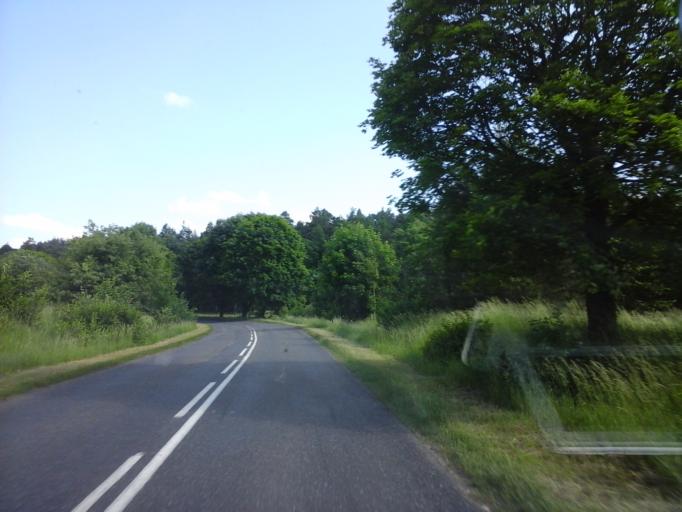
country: PL
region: Lubusz
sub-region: Powiat strzelecko-drezdenecki
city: Dobiegniew
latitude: 52.9962
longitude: 15.7484
